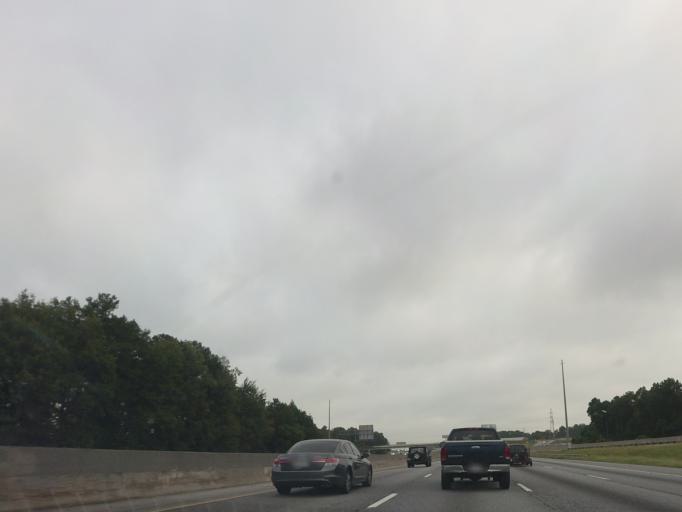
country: US
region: Georgia
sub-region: Clayton County
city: Riverdale
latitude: 33.5893
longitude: -84.3839
